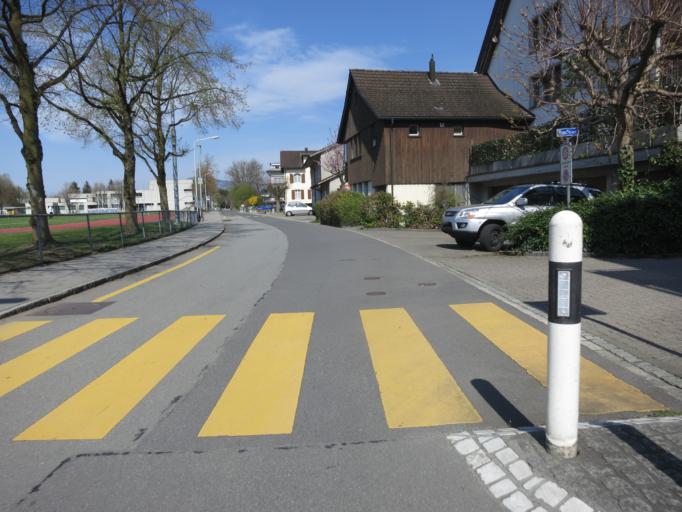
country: CH
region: Schwyz
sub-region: Bezirk March
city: Lachen
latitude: 47.1950
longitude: 8.8535
